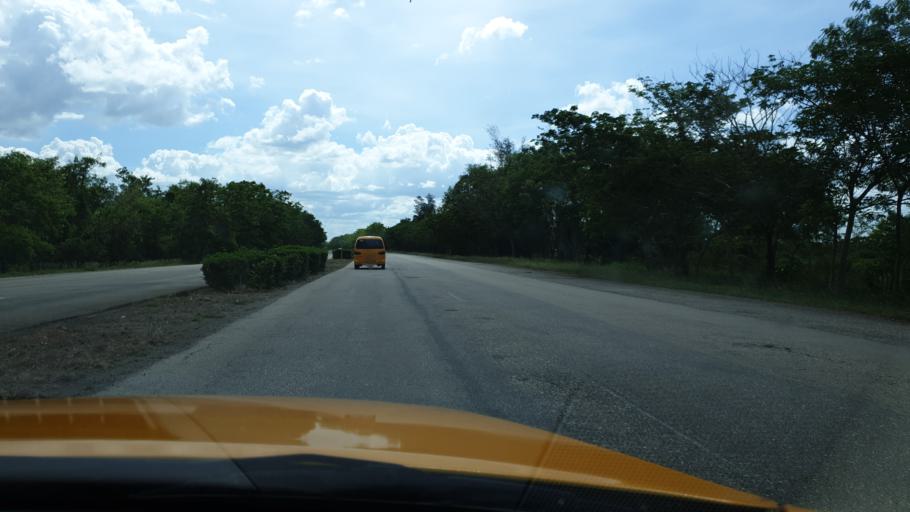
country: CU
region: Cienfuegos
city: Cruces
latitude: 22.4549
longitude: -80.3038
